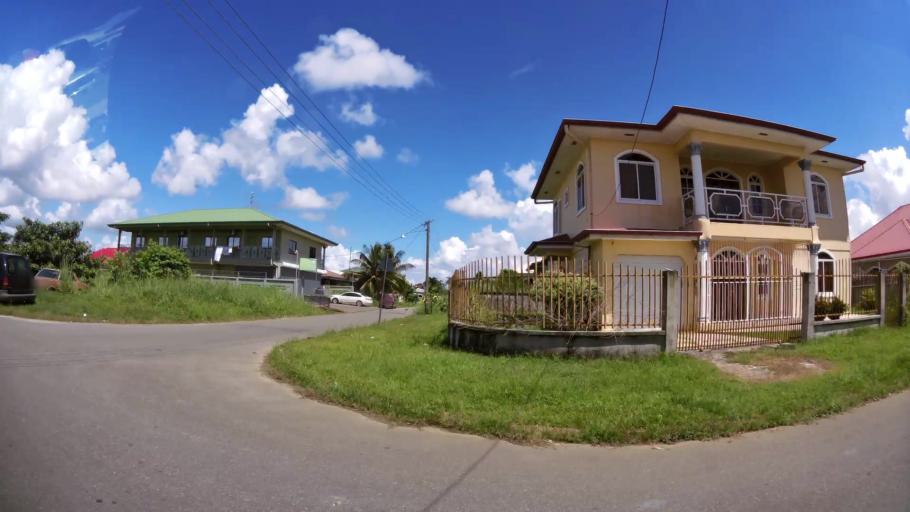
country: SR
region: Paramaribo
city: Paramaribo
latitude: 5.8646
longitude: -55.1434
